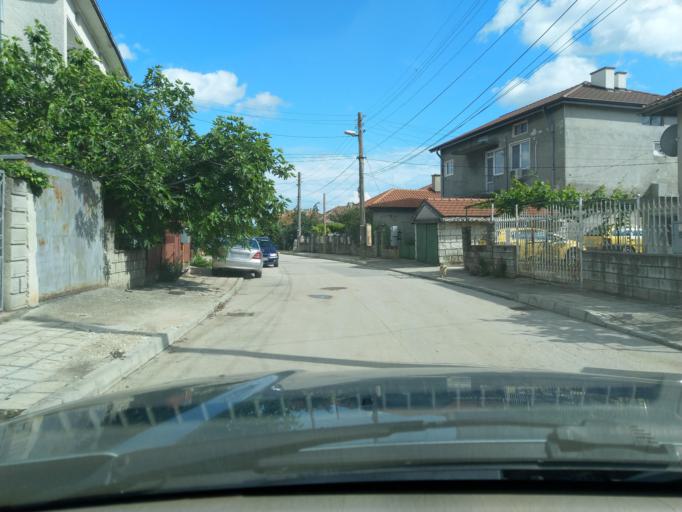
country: BG
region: Dobrich
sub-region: Obshtina Kavarna
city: Kavarna
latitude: 43.4332
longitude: 28.3317
